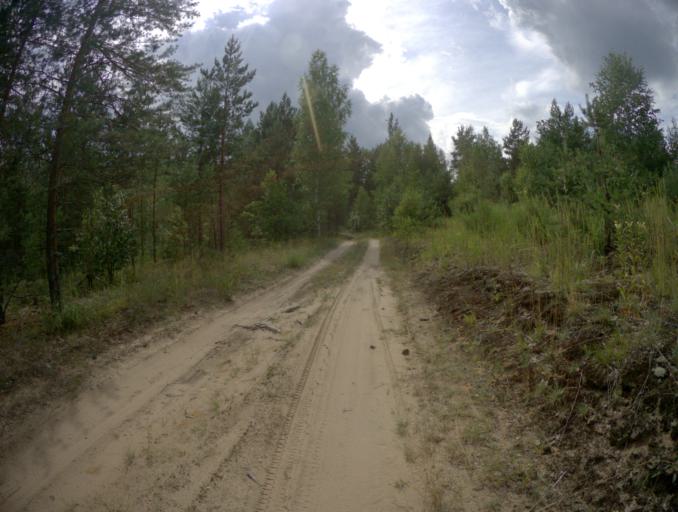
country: RU
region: Vladimir
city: Gorokhovets
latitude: 56.3000
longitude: 42.7043
